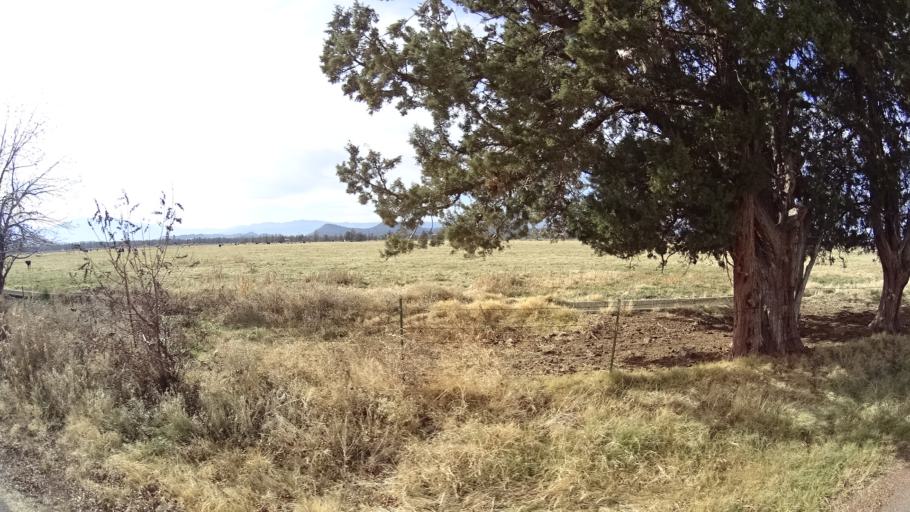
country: US
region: California
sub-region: Siskiyou County
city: Montague
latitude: 41.6040
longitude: -122.4044
